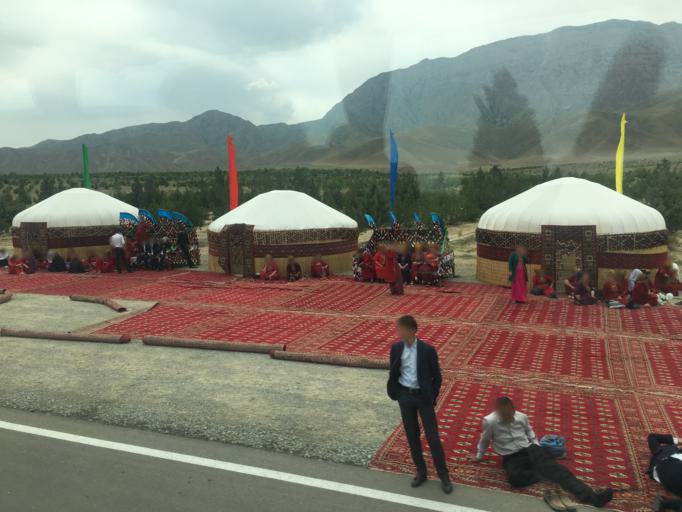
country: TM
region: Ahal
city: Abadan
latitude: 38.0394
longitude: 58.0825
